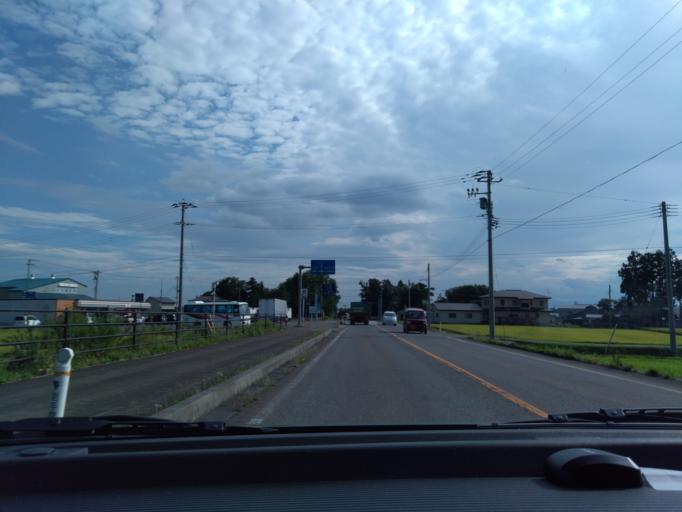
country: JP
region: Iwate
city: Hanamaki
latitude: 39.4620
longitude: 141.1016
